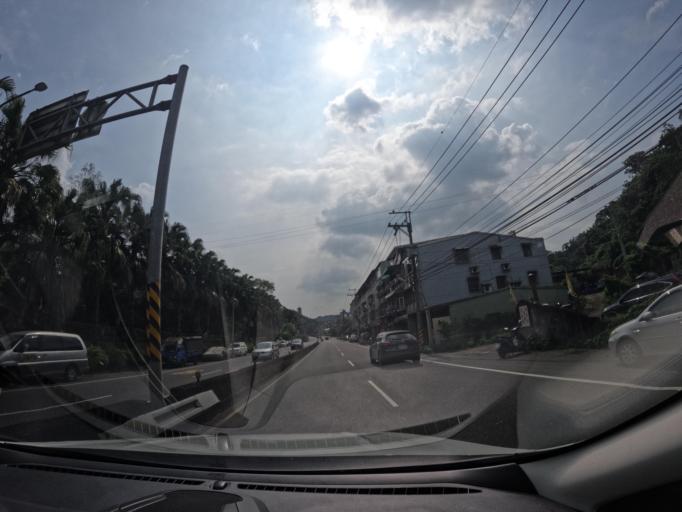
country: TW
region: Taiwan
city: Daxi
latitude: 24.9037
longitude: 121.3538
